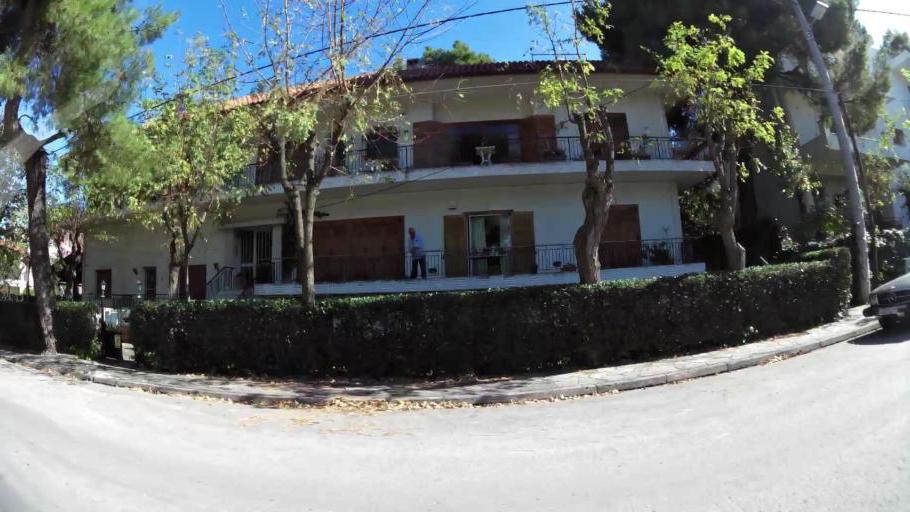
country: GR
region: Attica
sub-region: Nomarchia Anatolikis Attikis
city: Drosia
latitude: 38.1189
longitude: 23.8632
